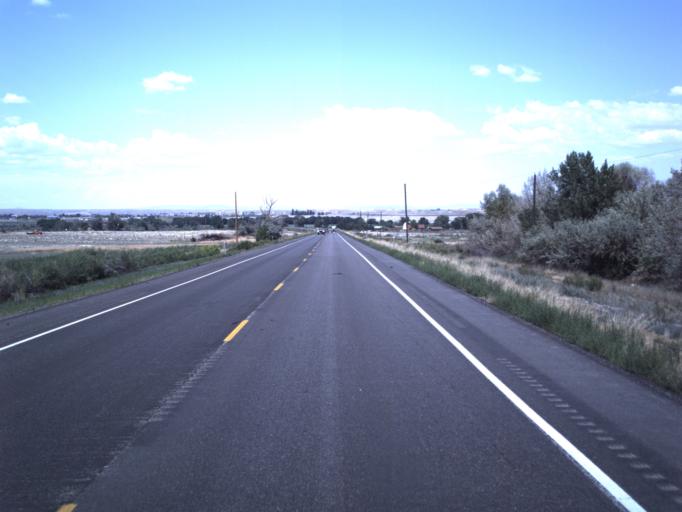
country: US
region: Utah
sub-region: Emery County
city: Huntington
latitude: 39.2875
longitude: -110.9715
